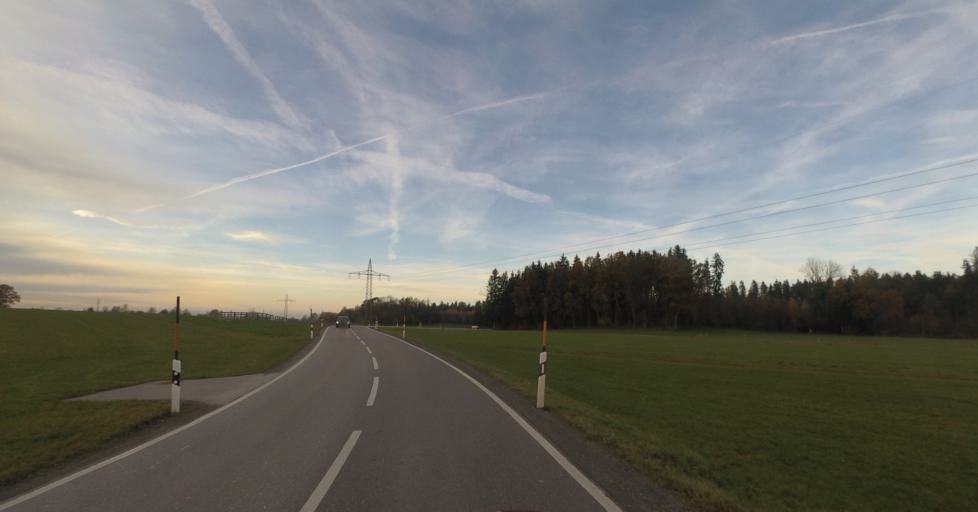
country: DE
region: Bavaria
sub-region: Upper Bavaria
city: Vachendorf
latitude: 47.8715
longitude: 12.6107
